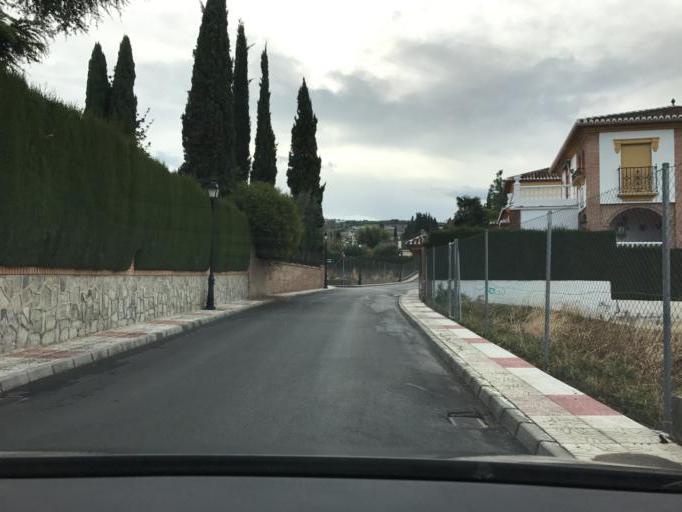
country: ES
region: Andalusia
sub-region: Provincia de Granada
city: Cajar
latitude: 37.1361
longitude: -3.5705
